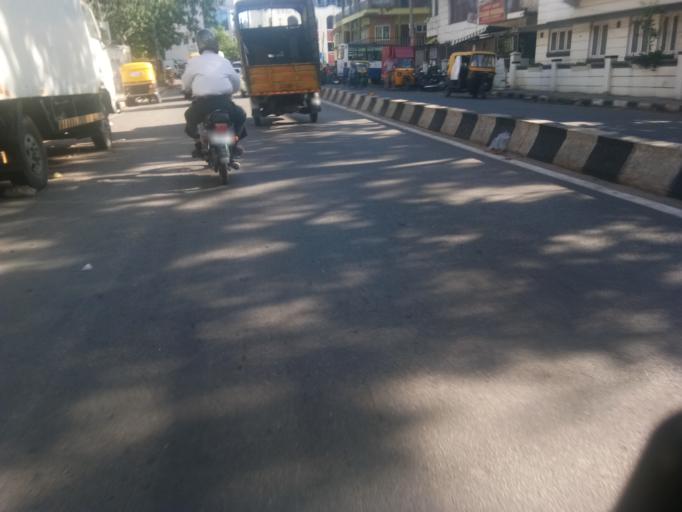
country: IN
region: Karnataka
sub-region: Bangalore Urban
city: Bangalore
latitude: 13.0167
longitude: 77.5980
